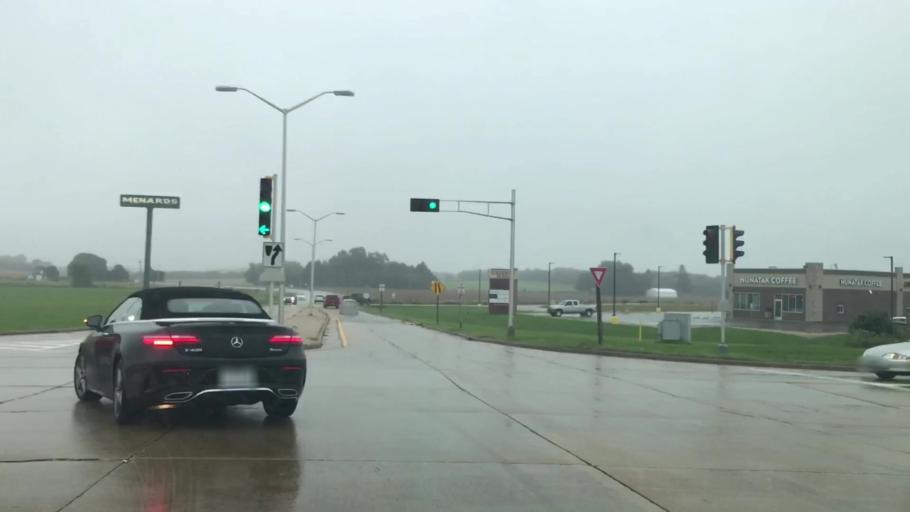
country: US
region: Wisconsin
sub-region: Dodge County
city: Beaver Dam
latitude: 43.4857
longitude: -88.8105
